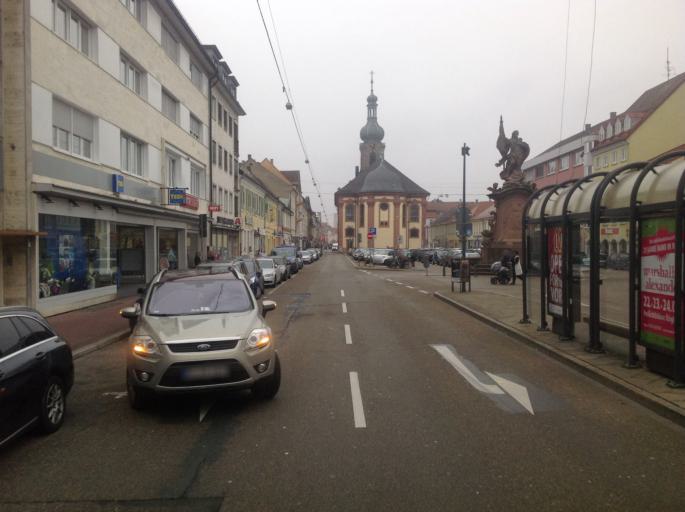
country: DE
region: Baden-Wuerttemberg
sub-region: Karlsruhe Region
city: Rastatt
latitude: 48.8557
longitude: 8.2043
